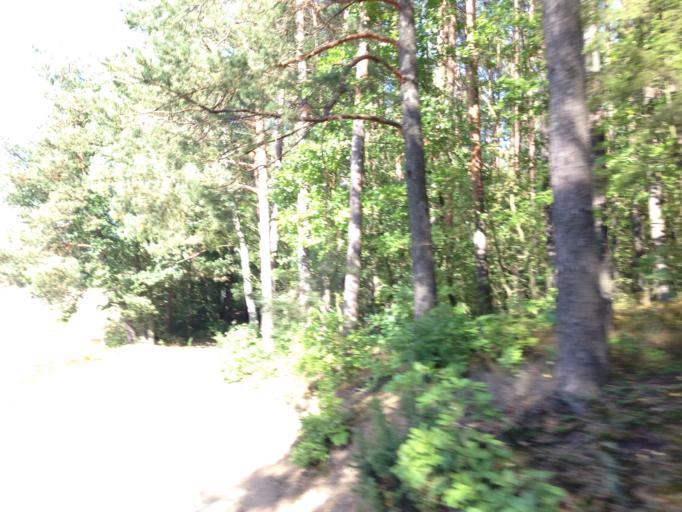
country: PL
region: Warmian-Masurian Voivodeship
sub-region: Powiat dzialdowski
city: Lidzbark
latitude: 53.2238
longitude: 19.7493
